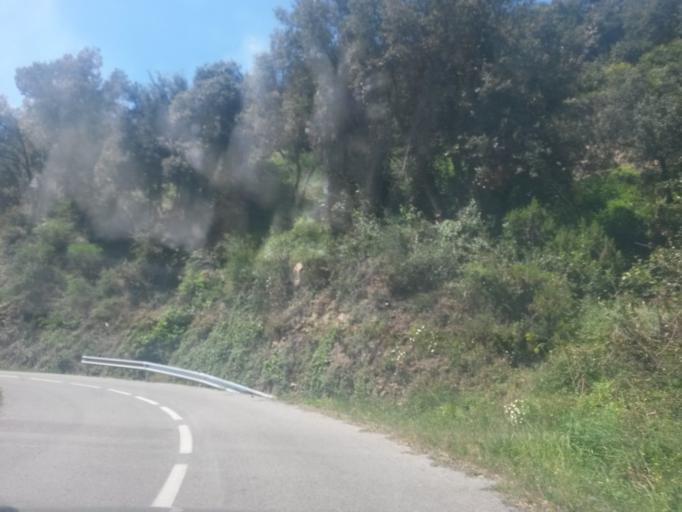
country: ES
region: Catalonia
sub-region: Provincia de Girona
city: Cassa de la Selva
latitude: 41.9258
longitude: 2.9154
